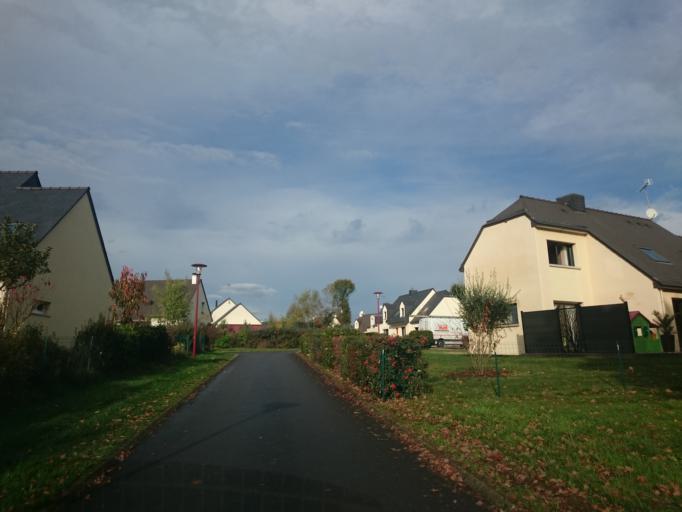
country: FR
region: Brittany
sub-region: Departement d'Ille-et-Vilaine
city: Bourg-des-Comptes
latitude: 47.9288
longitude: -1.7502
